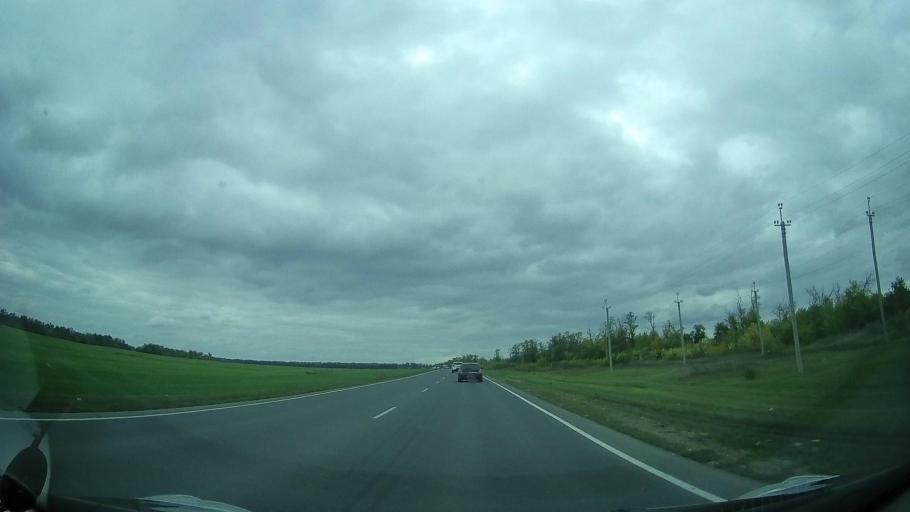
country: RU
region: Rostov
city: Yegorlykskaya
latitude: 46.5751
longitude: 40.6317
